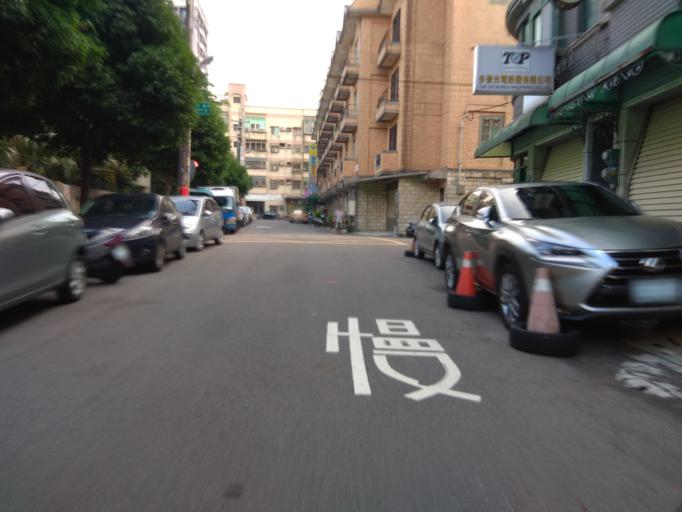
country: TW
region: Taiwan
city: Daxi
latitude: 24.9439
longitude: 121.2022
